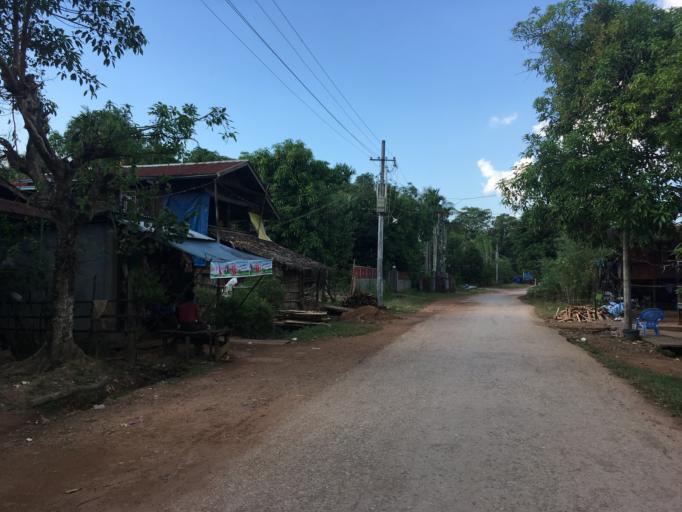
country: MM
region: Mon
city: Mawlamyine
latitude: 16.4355
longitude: 97.6205
